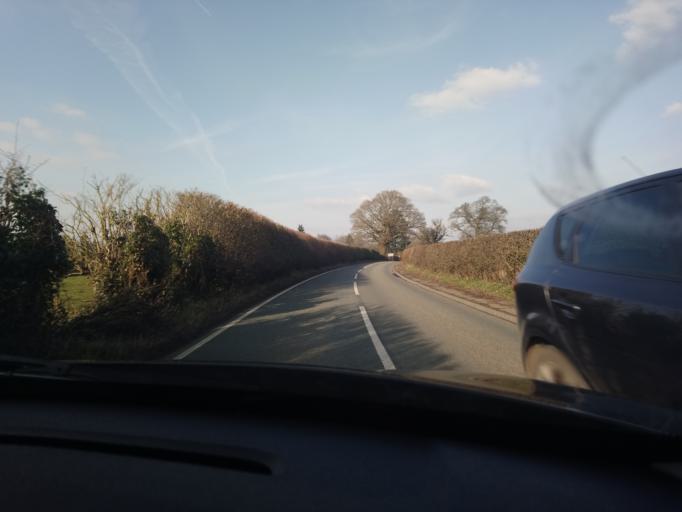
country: GB
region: England
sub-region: Shropshire
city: Bicton
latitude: 52.7501
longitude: -2.7801
